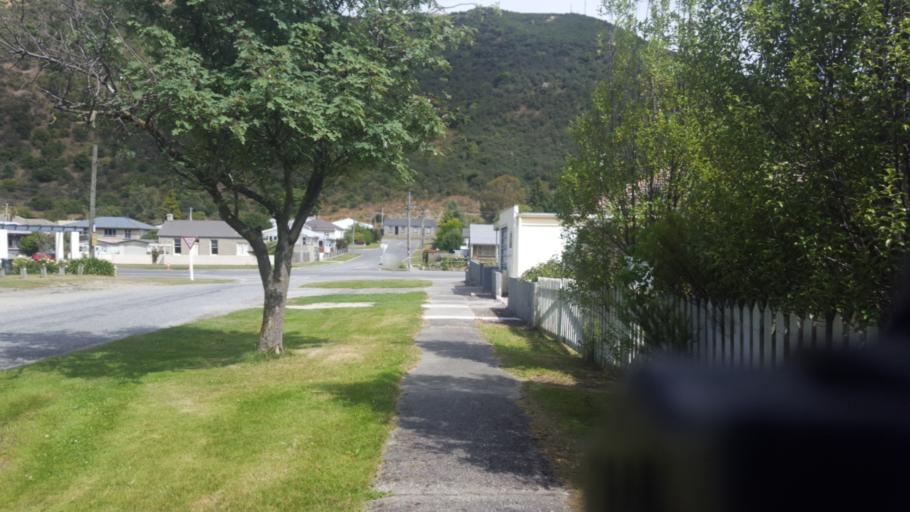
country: NZ
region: Otago
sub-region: Queenstown-Lakes District
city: Kingston
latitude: -45.5443
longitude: 169.3149
